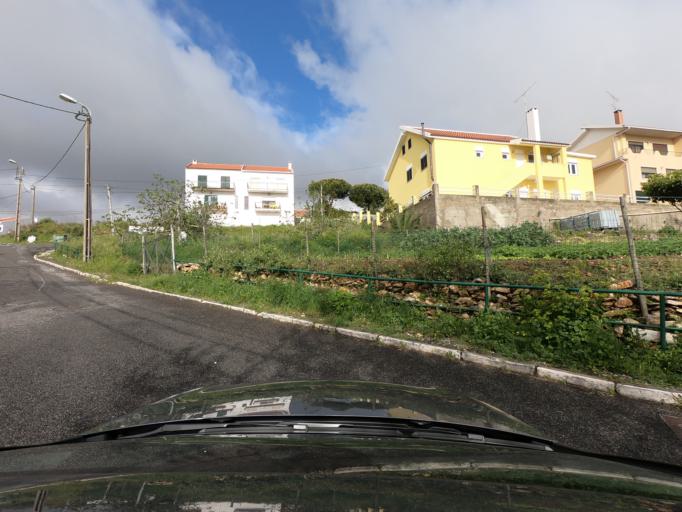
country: PT
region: Lisbon
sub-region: Oeiras
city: Porto Salvo
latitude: 38.7256
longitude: -9.3099
